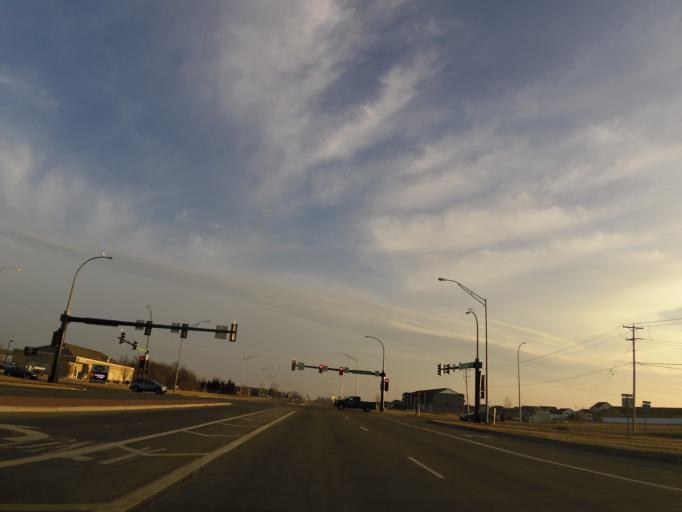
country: US
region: North Dakota
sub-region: Grand Forks County
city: Grand Forks
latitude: 47.8754
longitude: -97.0455
